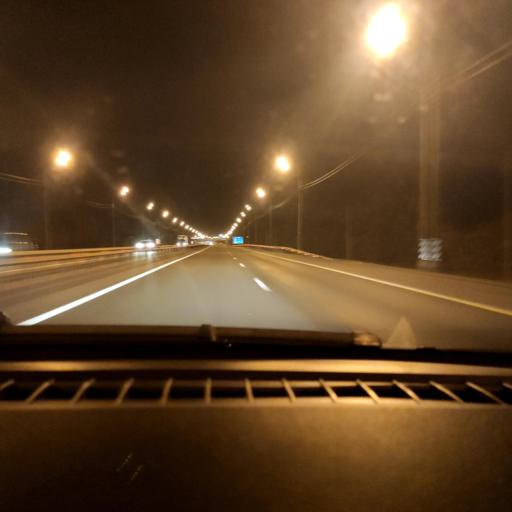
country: RU
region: Lipetsk
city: Khlevnoye
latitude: 52.2053
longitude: 39.1598
